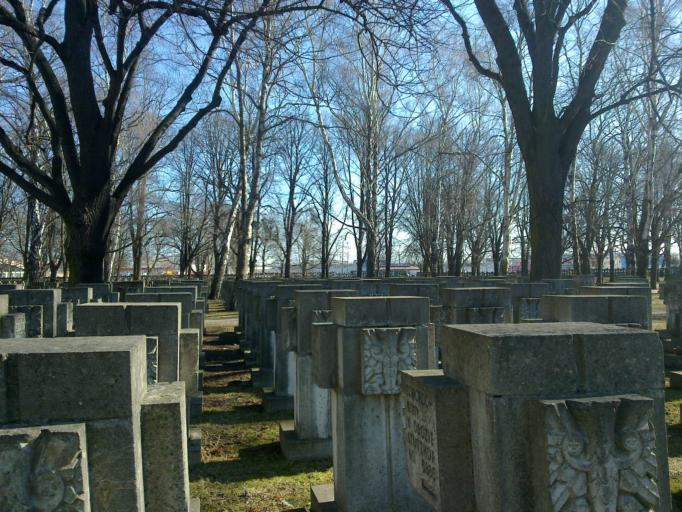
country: PL
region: Pomeranian Voivodeship
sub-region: Gdansk
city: Gdansk
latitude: 54.3931
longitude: 18.6151
